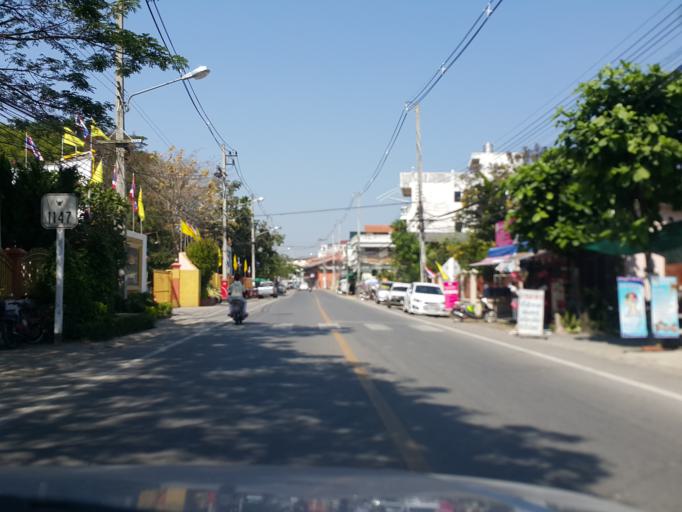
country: TH
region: Chiang Mai
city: San Kamphaeng
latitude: 18.7399
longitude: 99.1246
